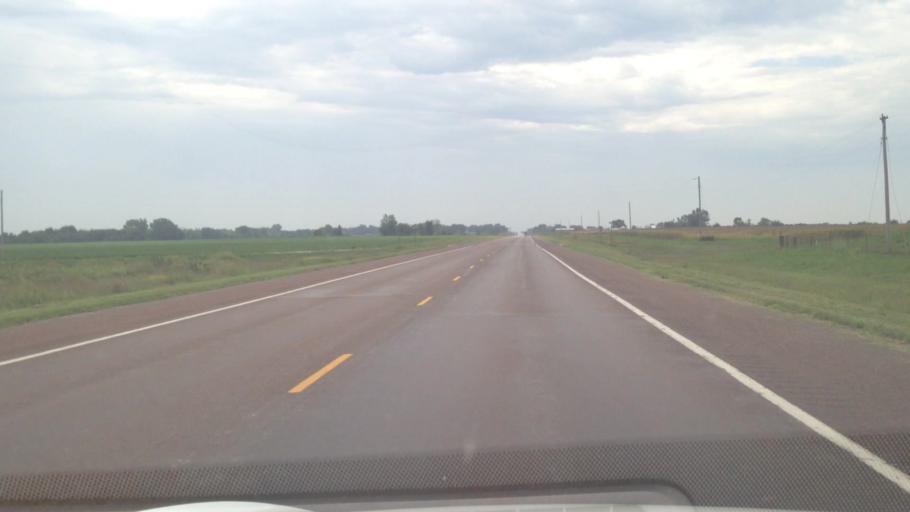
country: US
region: Kansas
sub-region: Crawford County
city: Girard
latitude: 37.4563
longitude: -94.8330
